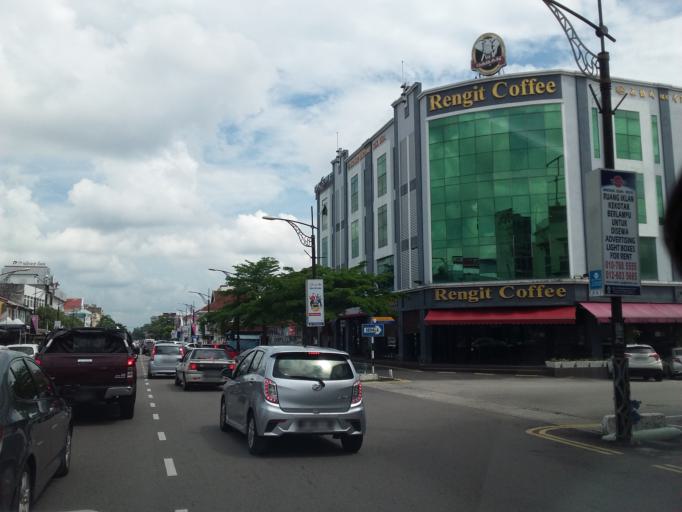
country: MY
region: Johor
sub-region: Daerah Batu Pahat
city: Batu Pahat
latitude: 1.8488
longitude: 102.9314
